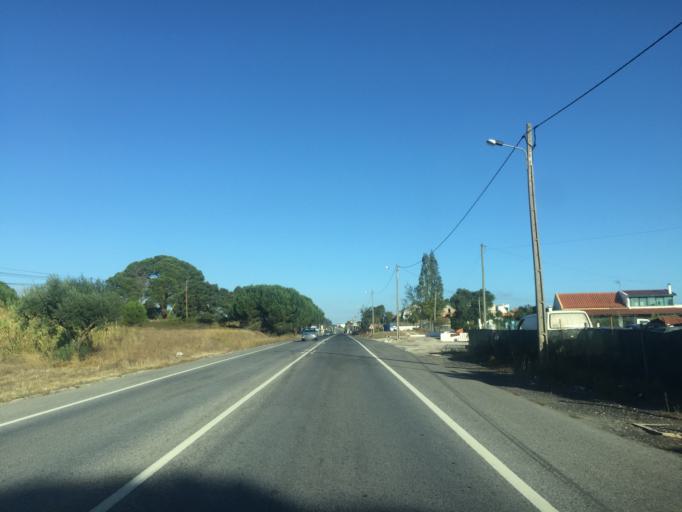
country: PT
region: Lisbon
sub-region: Azambuja
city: Aveiras de Cima
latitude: 39.1517
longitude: -8.9097
